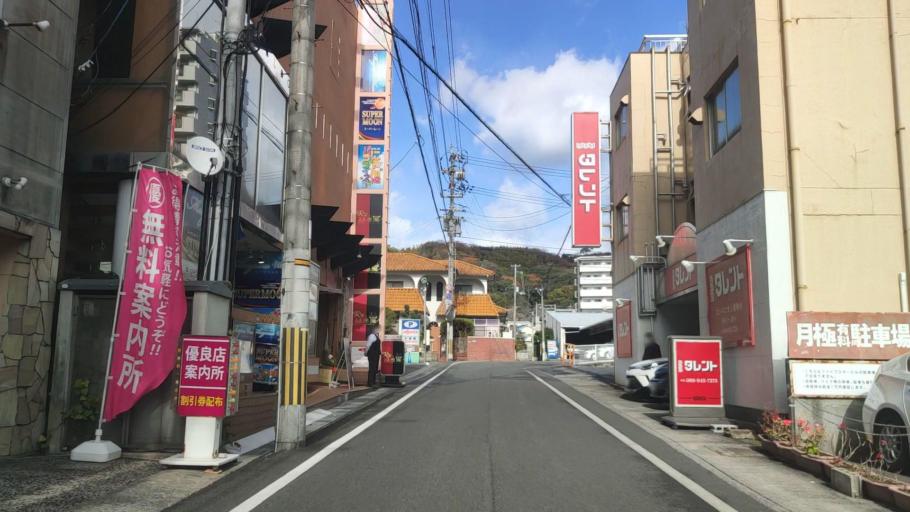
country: JP
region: Ehime
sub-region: Shikoku-chuo Shi
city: Matsuyama
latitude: 33.8540
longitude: 132.7837
